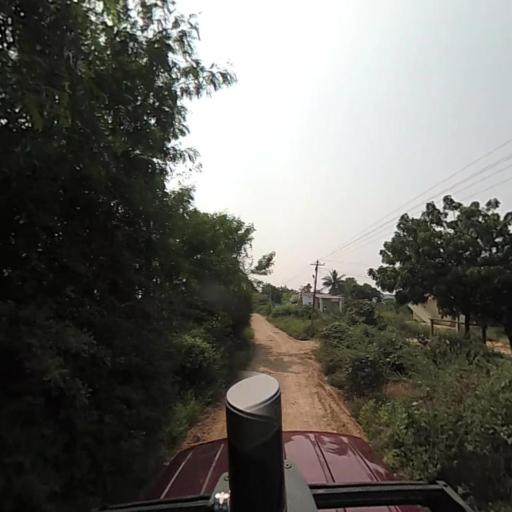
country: IN
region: Telangana
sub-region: Nalgonda
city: Nalgonda
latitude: 17.1932
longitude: 79.1332
